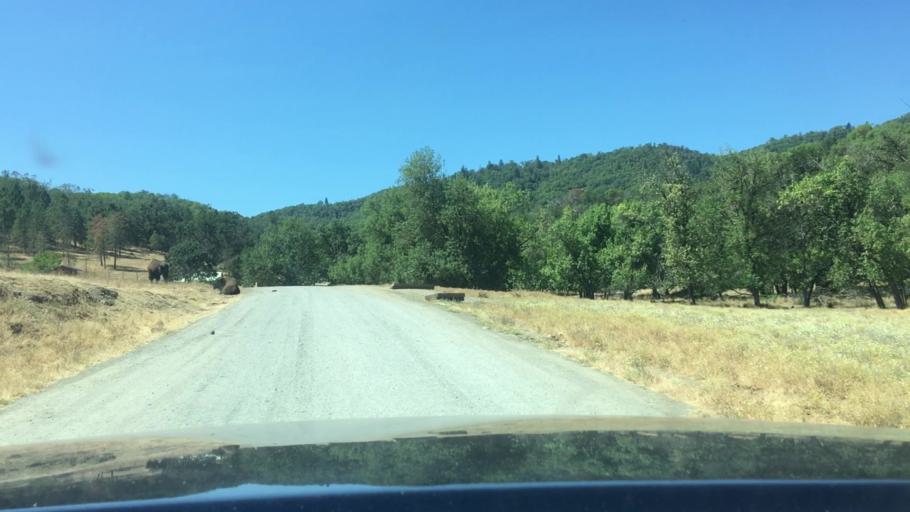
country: US
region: Oregon
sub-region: Douglas County
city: Winston
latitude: 43.1316
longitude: -123.4356
